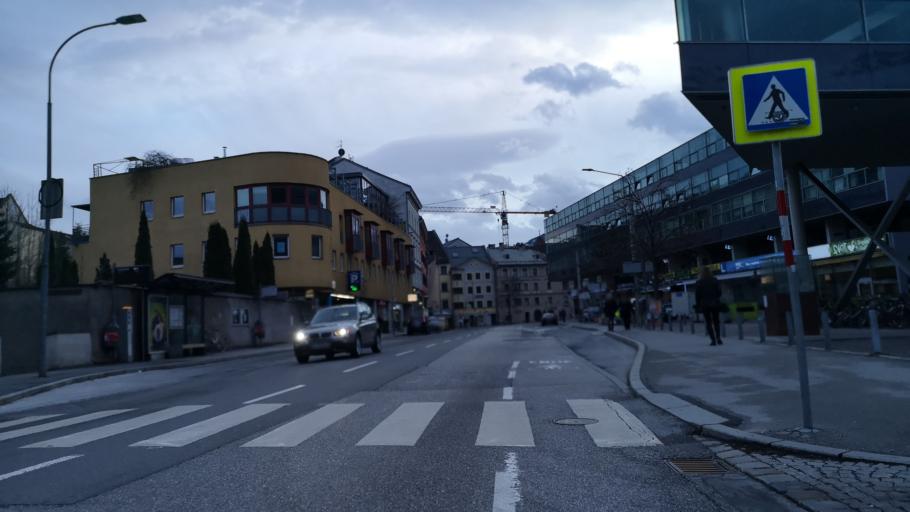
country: AT
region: Tyrol
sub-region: Innsbruck Stadt
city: Innsbruck
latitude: 47.2702
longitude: 11.3998
